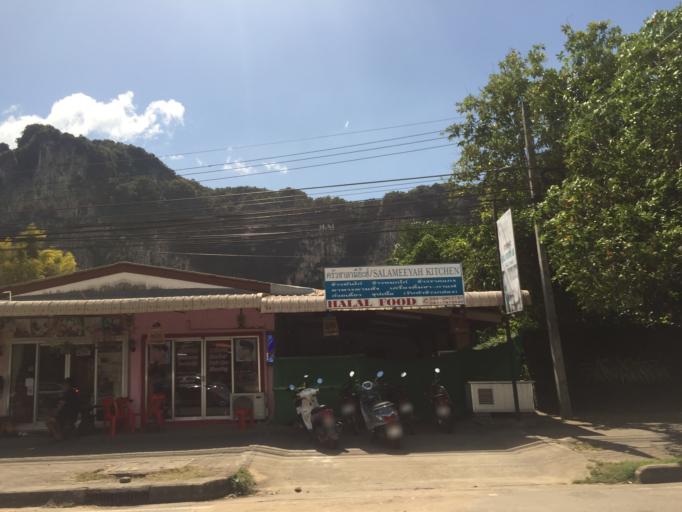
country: TH
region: Phangnga
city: Ban Ao Nang
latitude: 8.0352
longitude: 98.8319
